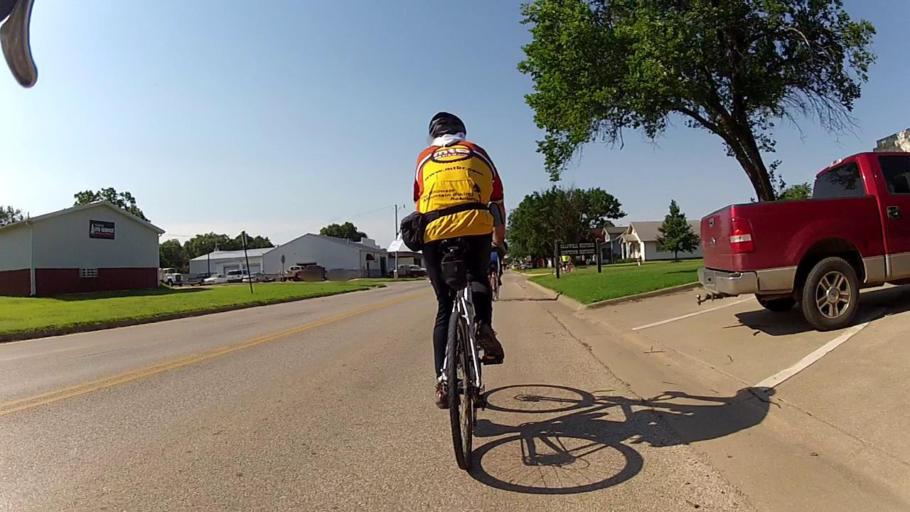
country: US
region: Kansas
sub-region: Sumner County
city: Caldwell
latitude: 37.0350
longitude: -97.6070
